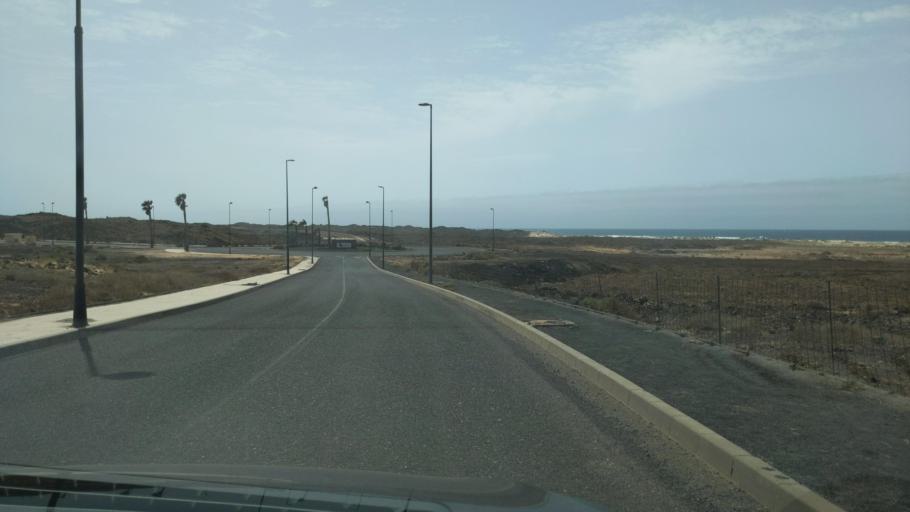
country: ES
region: Canary Islands
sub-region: Provincia de Las Palmas
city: Corralejo
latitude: 28.7375
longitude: -13.9433
